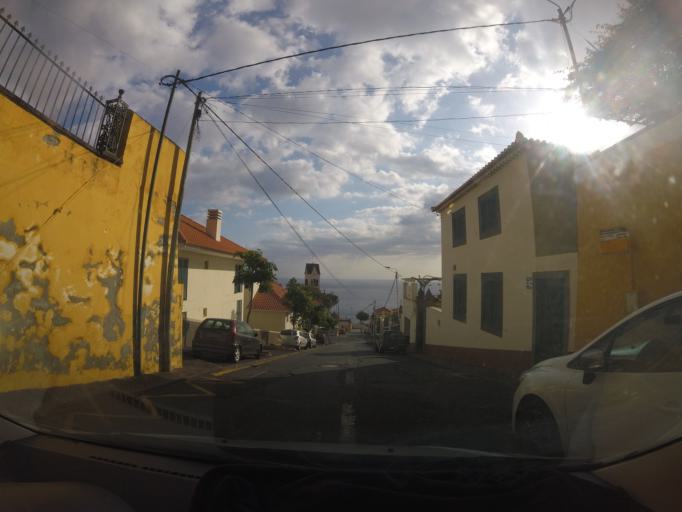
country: PT
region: Madeira
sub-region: Funchal
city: Nossa Senhora do Monte
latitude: 32.6505
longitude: -16.8821
